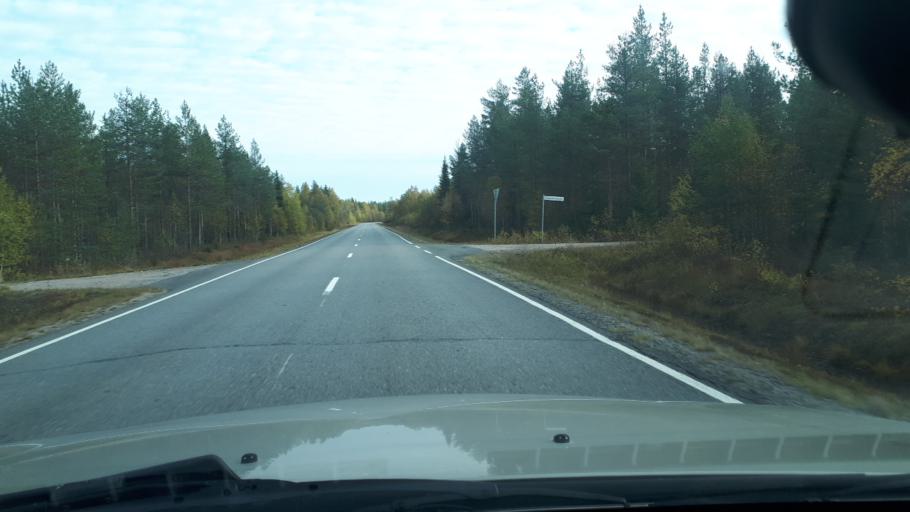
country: FI
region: Northern Ostrobothnia
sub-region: Oulu
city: Yli-Ii
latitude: 65.9221
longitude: 25.8040
